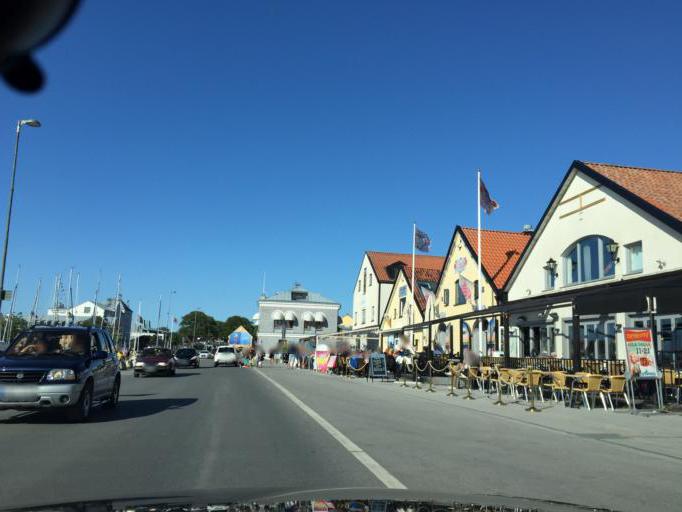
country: SE
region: Gotland
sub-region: Gotland
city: Visby
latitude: 57.6370
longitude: 18.2867
